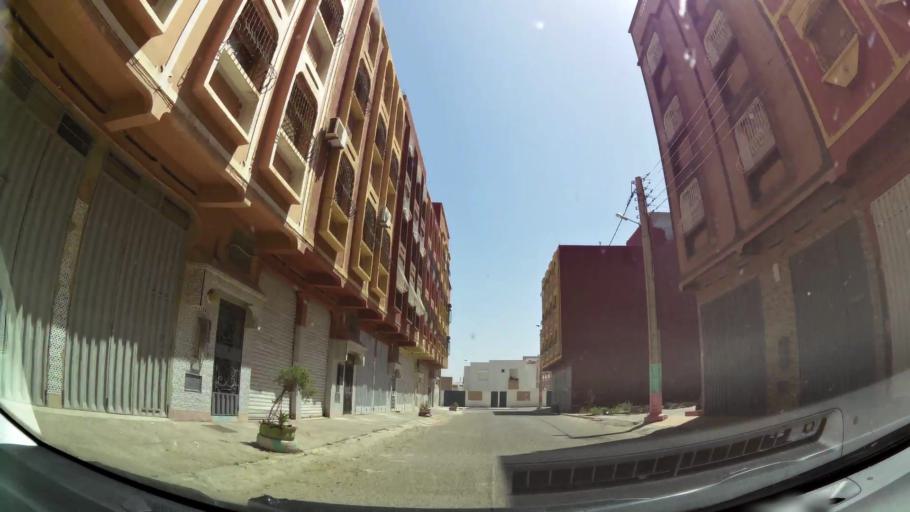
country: MA
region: Souss-Massa-Draa
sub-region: Inezgane-Ait Mellou
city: Inezgane
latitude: 30.3343
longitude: -9.5006
